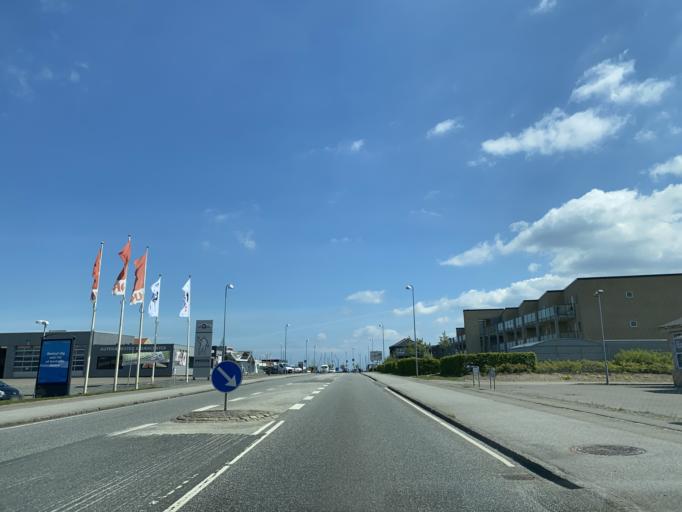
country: DK
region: South Denmark
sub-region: Aabenraa Kommune
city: Aabenraa
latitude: 55.0349
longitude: 9.4176
